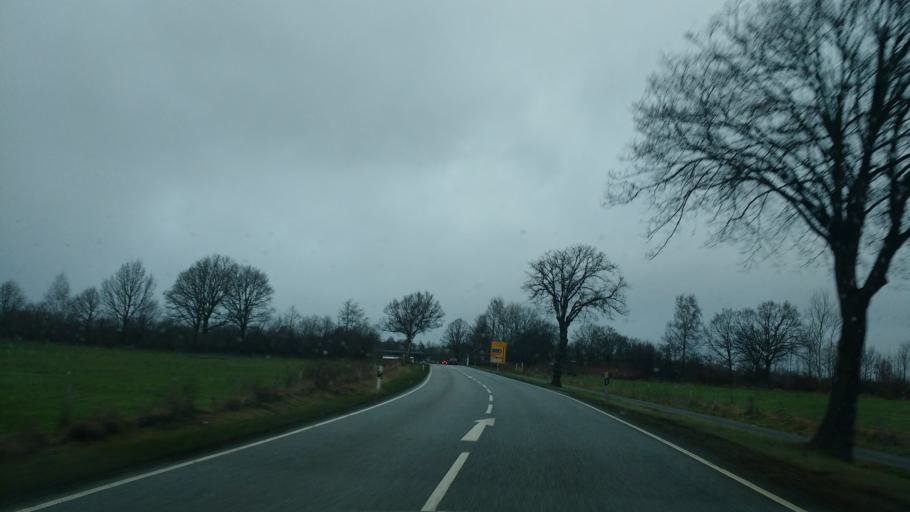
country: DE
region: Schleswig-Holstein
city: Grauel
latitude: 54.0741
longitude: 9.6508
